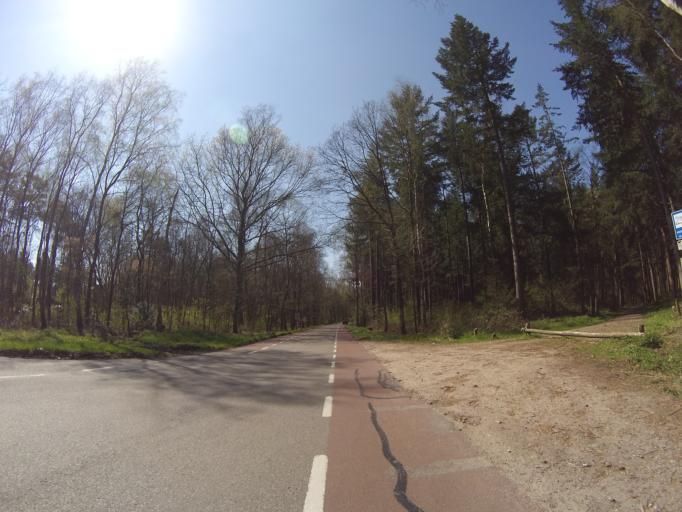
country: NL
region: Utrecht
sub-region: Gemeente Utrechtse Heuvelrug
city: Overberg
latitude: 52.0311
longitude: 5.4882
